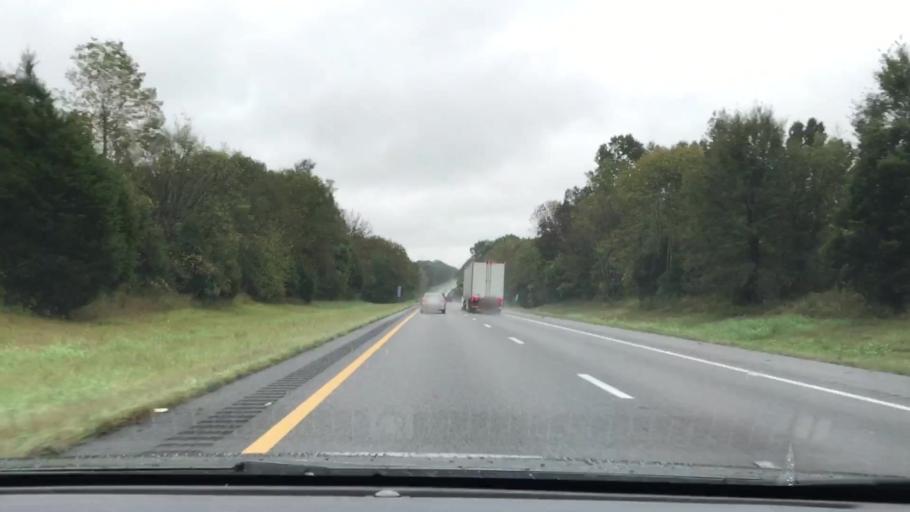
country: US
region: Tennessee
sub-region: Cheatham County
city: Pleasant View
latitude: 36.4707
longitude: -87.1319
